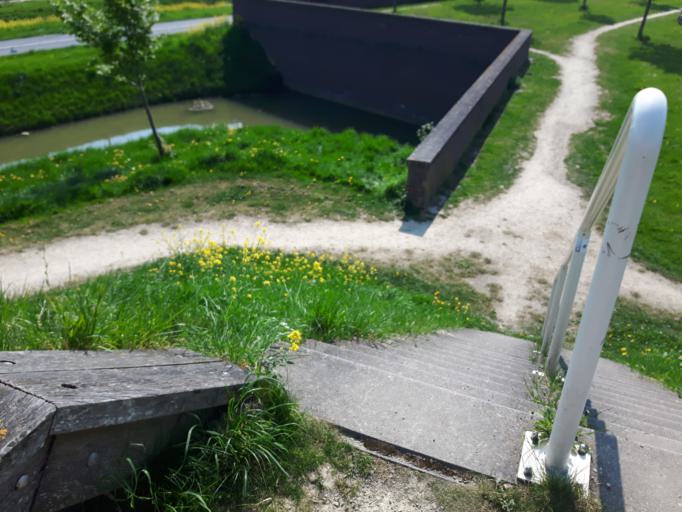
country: NL
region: Utrecht
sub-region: Gemeente Houten
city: Houten
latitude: 52.0116
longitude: 5.1879
